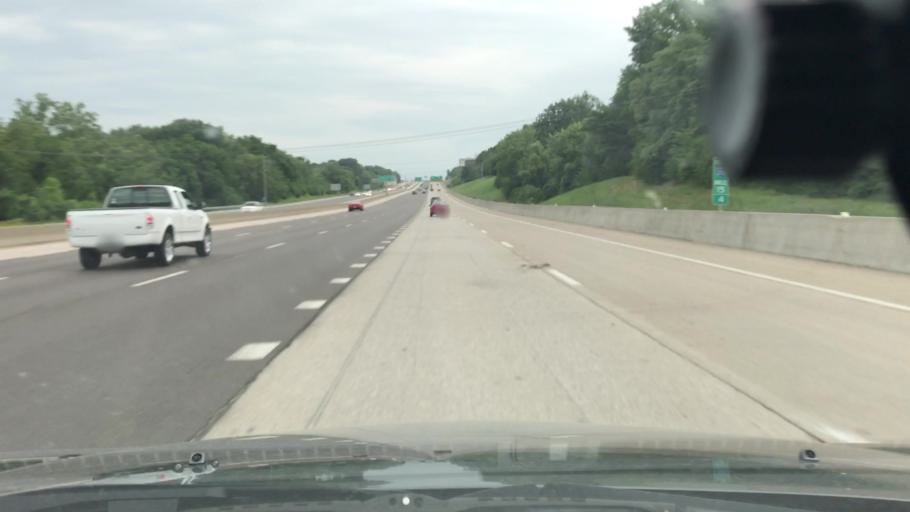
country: US
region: Missouri
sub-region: Saint Louis County
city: Creve Coeur
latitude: 38.6808
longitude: -90.4495
